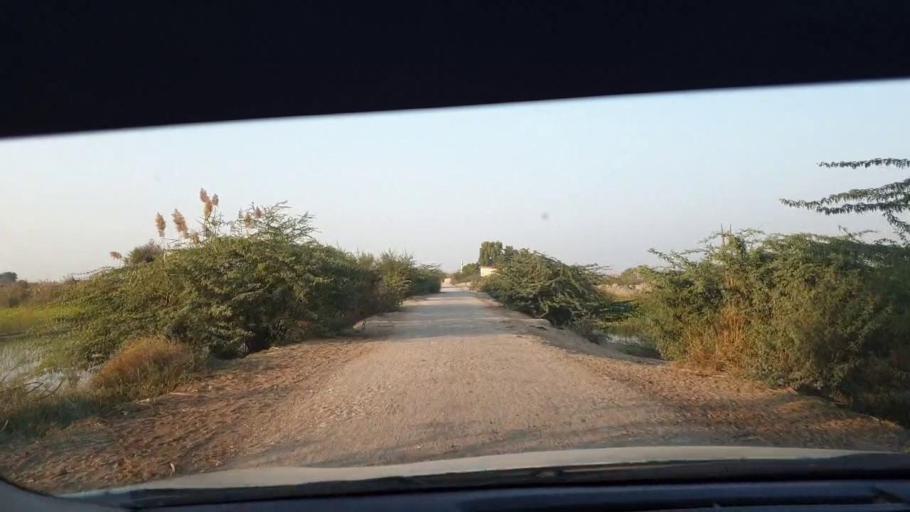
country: PK
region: Sindh
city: Berani
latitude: 25.8577
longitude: 68.8164
